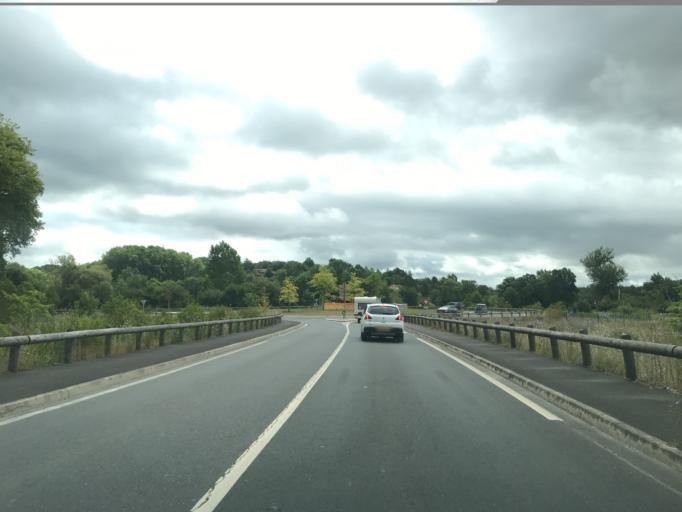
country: FR
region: Aquitaine
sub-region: Departement de la Dordogne
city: Mareuil
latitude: 45.4823
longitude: 0.3752
